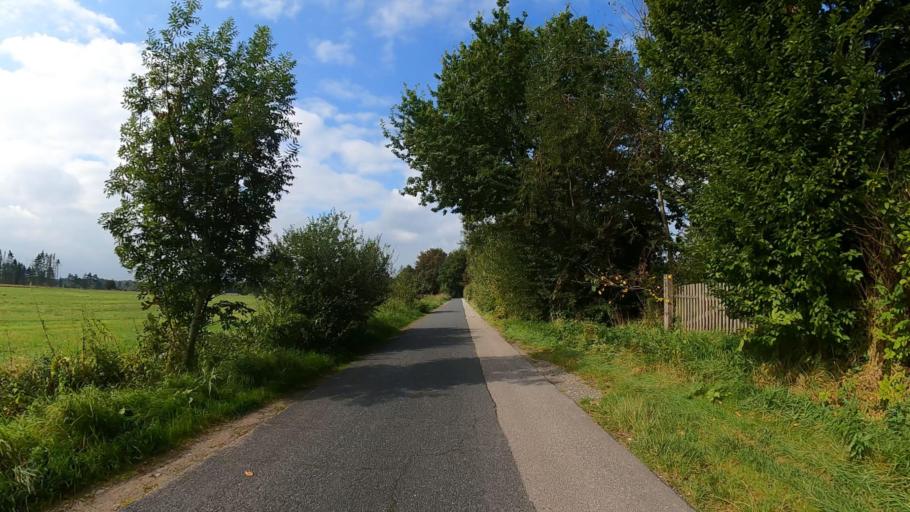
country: DE
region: Schleswig-Holstein
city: Tornesch
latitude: 53.7208
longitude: 9.7013
